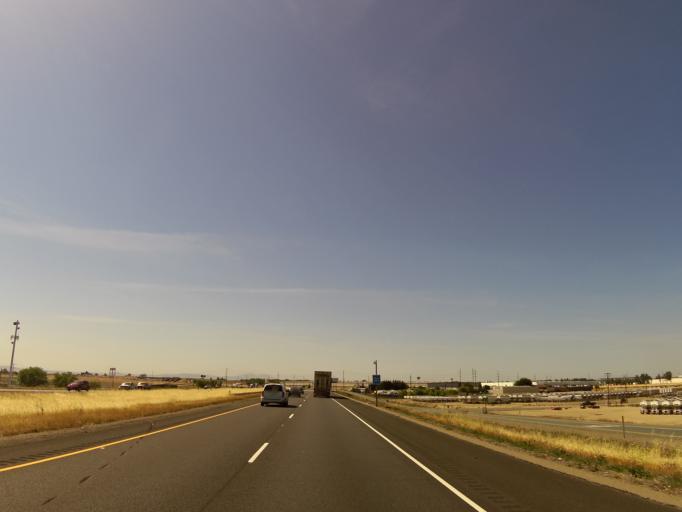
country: US
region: California
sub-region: San Joaquin County
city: Lathrop
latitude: 37.7889
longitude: -121.2848
